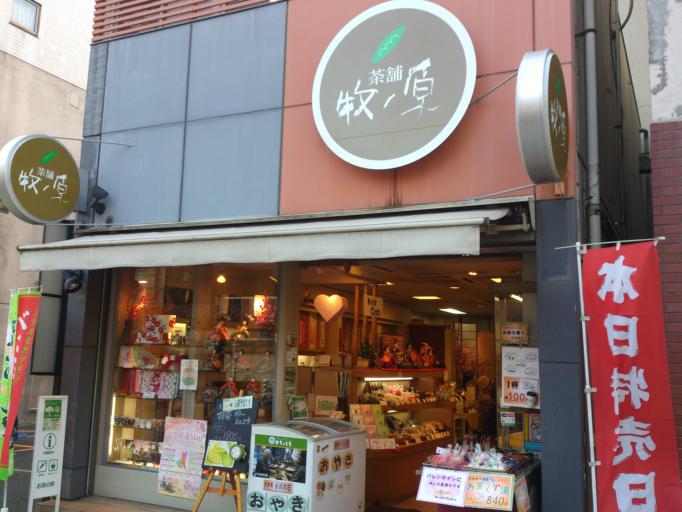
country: JP
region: Ibaraki
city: Mito-shi
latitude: 36.3740
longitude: 140.4738
